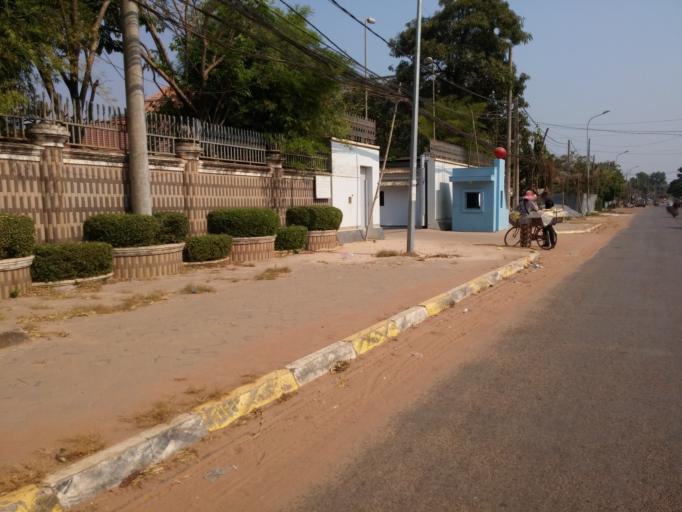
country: KH
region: Siem Reap
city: Siem Reap
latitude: 13.3710
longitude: 103.8495
